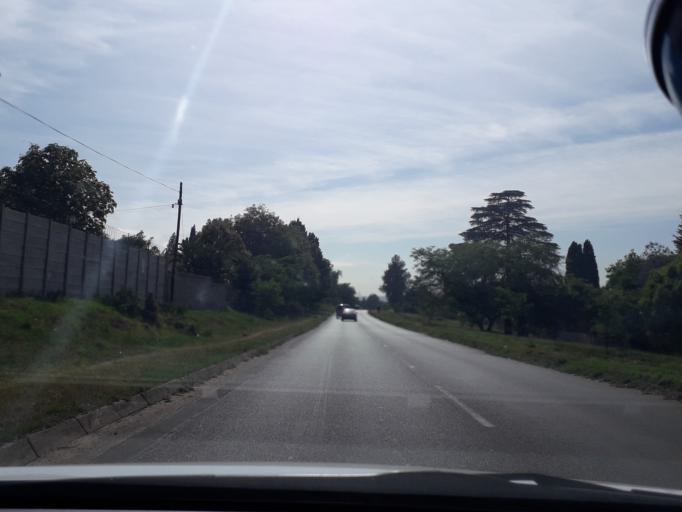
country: ZA
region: Gauteng
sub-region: City of Johannesburg Metropolitan Municipality
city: Roodepoort
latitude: -26.1189
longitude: 27.9283
